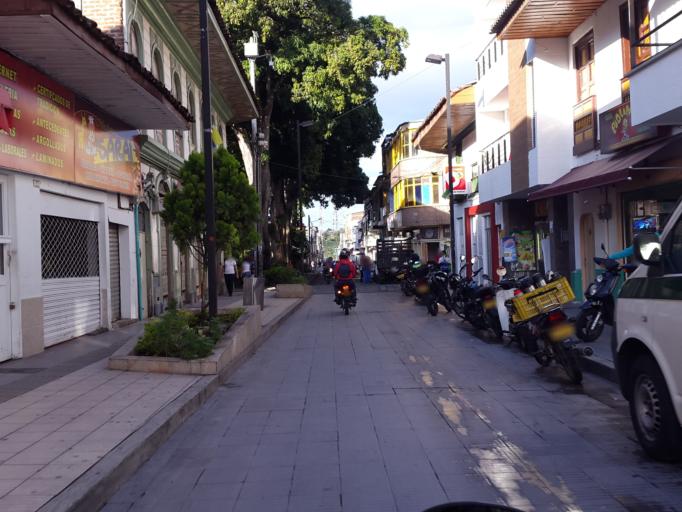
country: CO
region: Quindio
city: Montenegro
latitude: 4.5676
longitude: -75.7500
